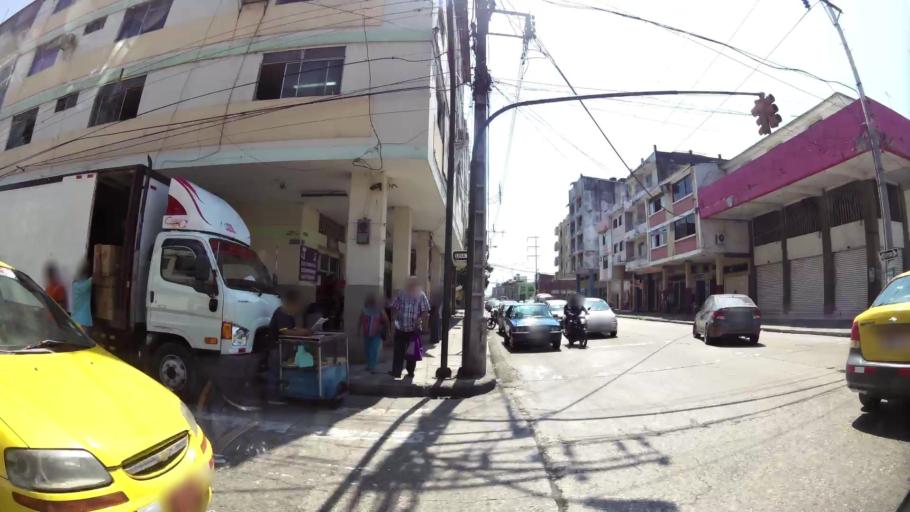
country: EC
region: Guayas
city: Guayaquil
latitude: -2.1951
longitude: -79.8947
